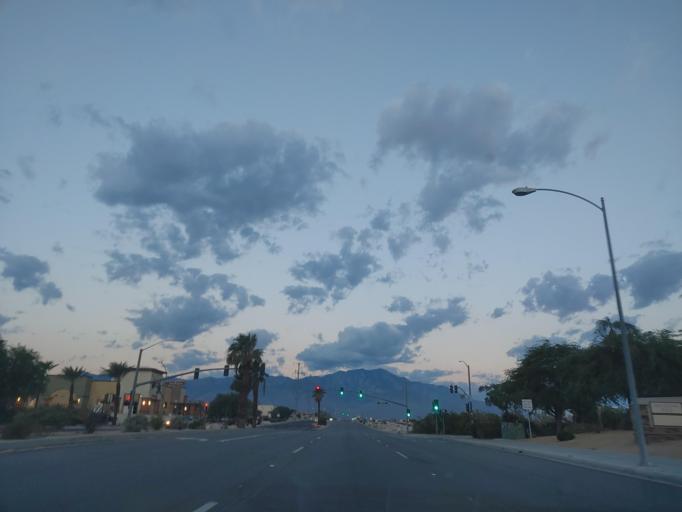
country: US
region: California
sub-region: Riverside County
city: Thousand Palms
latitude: 33.8019
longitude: -116.3917
